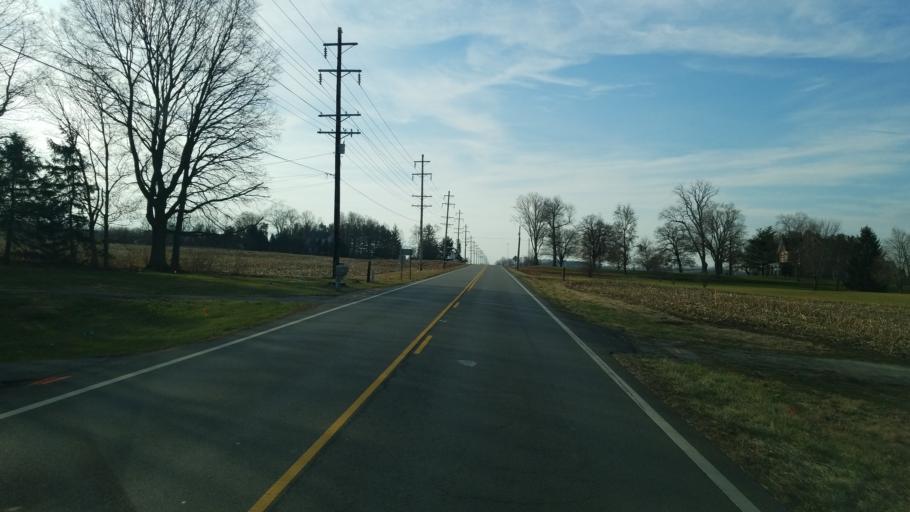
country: US
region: Ohio
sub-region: Ross County
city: Kingston
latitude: 39.4237
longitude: -82.9546
